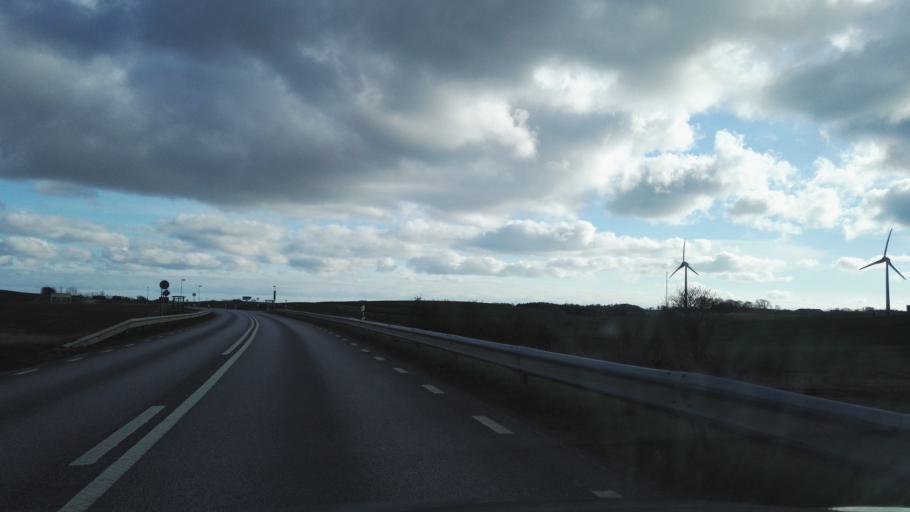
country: SE
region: Skane
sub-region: Ystads Kommun
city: Ystad
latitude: 55.4707
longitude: 13.7971
